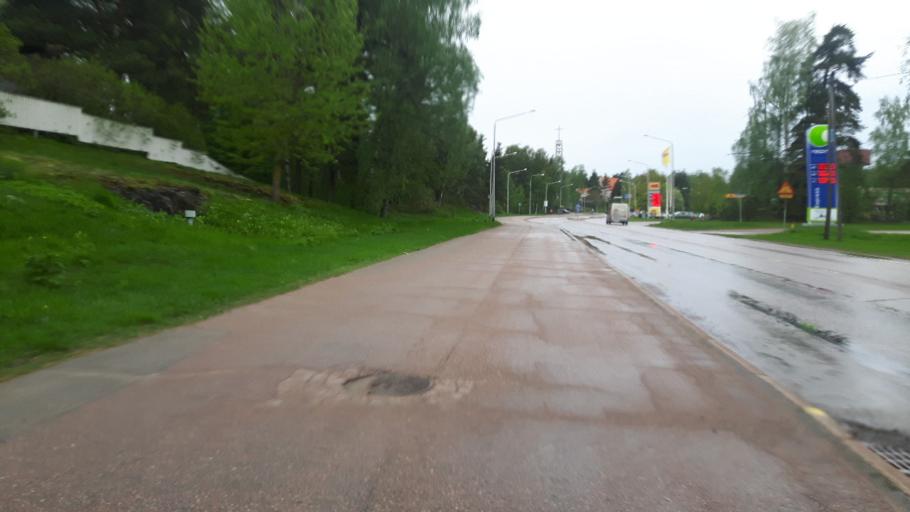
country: FI
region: Kymenlaakso
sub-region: Kotka-Hamina
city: Kotka
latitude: 60.4852
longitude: 26.9073
